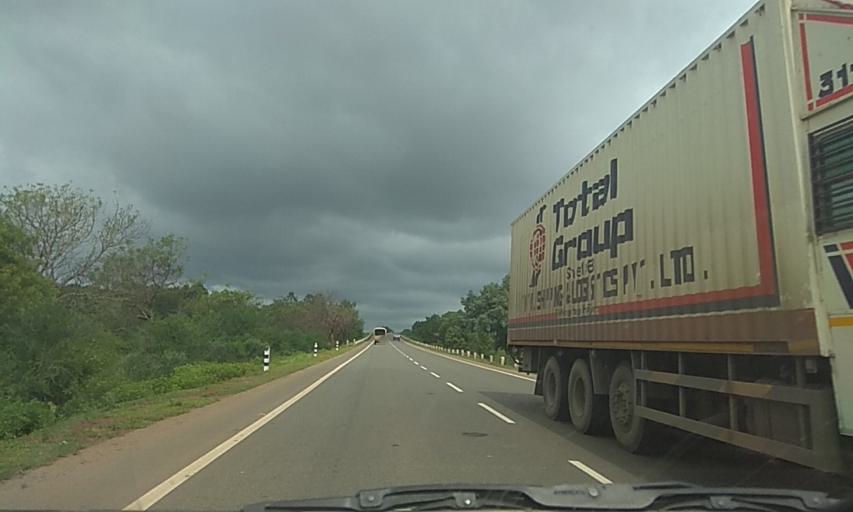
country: IN
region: Karnataka
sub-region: Dharwad
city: Hubli
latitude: 15.3404
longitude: 75.0837
